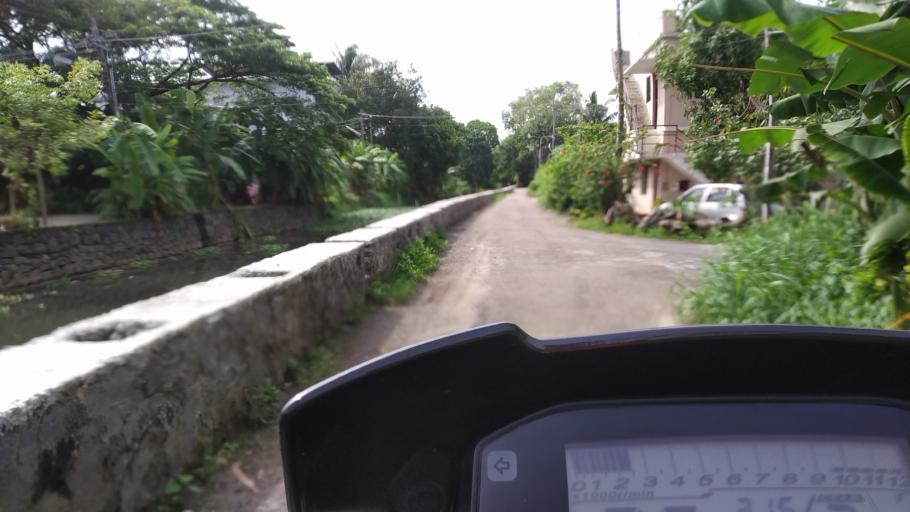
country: IN
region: Kerala
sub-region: Ernakulam
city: Cochin
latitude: 9.9813
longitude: 76.2915
